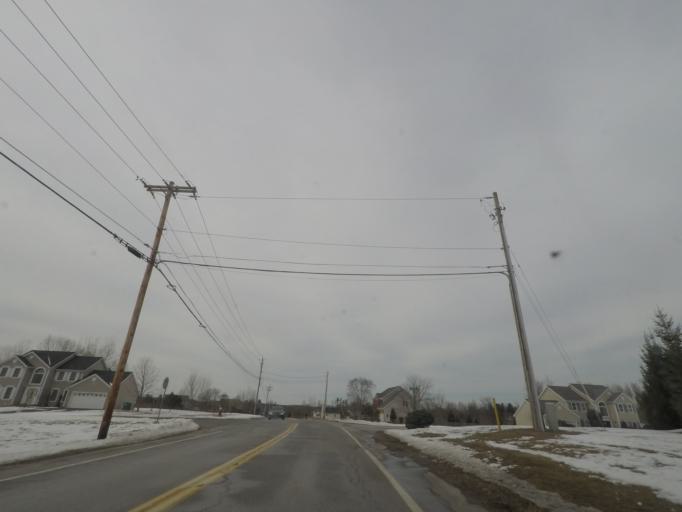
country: US
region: New York
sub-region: Albany County
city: Westmere
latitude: 42.6799
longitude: -73.8987
